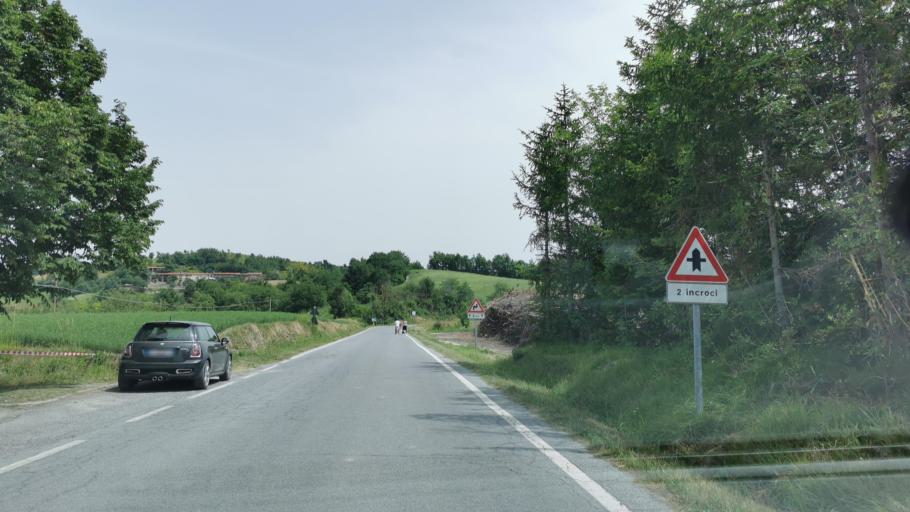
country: IT
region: Piedmont
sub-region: Provincia di Cuneo
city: Sale San Giovanni
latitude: 44.4046
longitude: 8.0755
